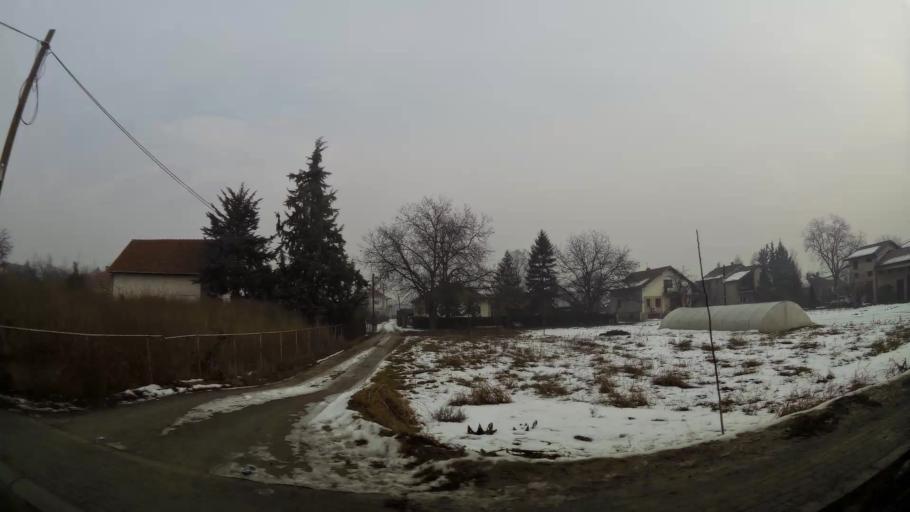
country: MK
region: Ilinden
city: Jurumleri
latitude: 41.9662
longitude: 21.5515
